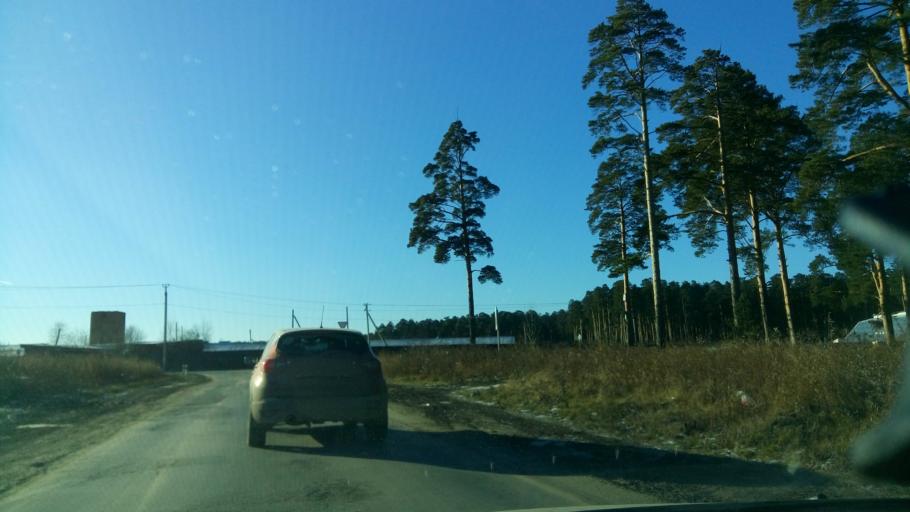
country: RU
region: Sverdlovsk
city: Gornyy Shchit
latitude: 56.7005
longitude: 60.5114
